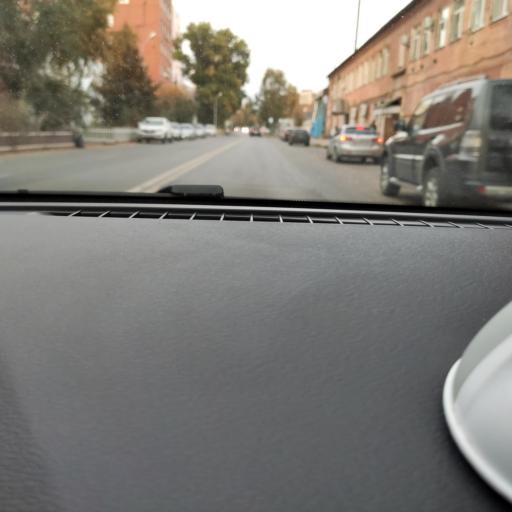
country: RU
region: Samara
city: Samara
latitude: 53.1821
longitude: 50.1057
